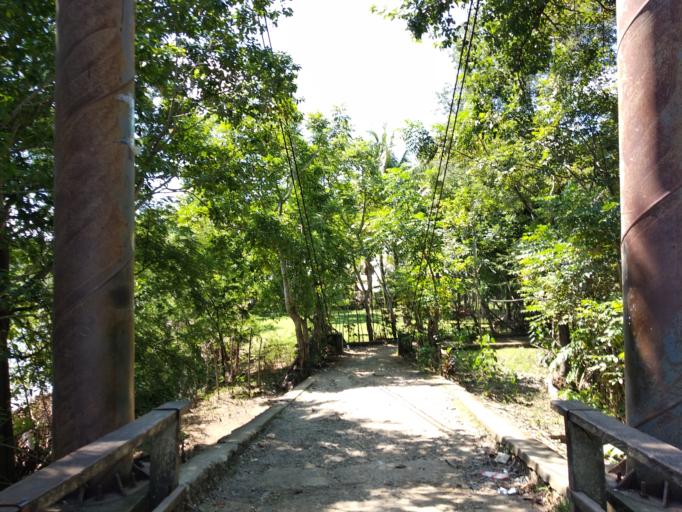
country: ID
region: South Sulawesi
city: Kadai
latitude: -4.7396
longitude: 120.3871
